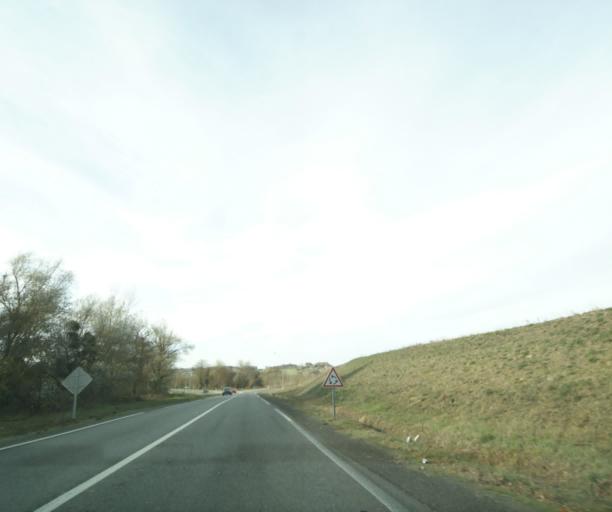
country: FR
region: Midi-Pyrenees
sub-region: Departement du Gers
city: Gimont
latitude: 43.6231
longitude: 0.9081
